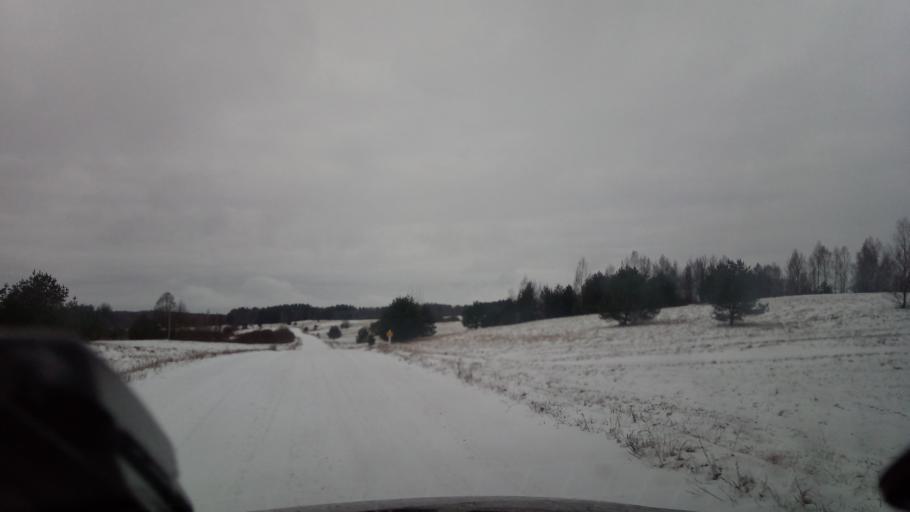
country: LT
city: Zarasai
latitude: 55.6846
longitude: 26.1046
